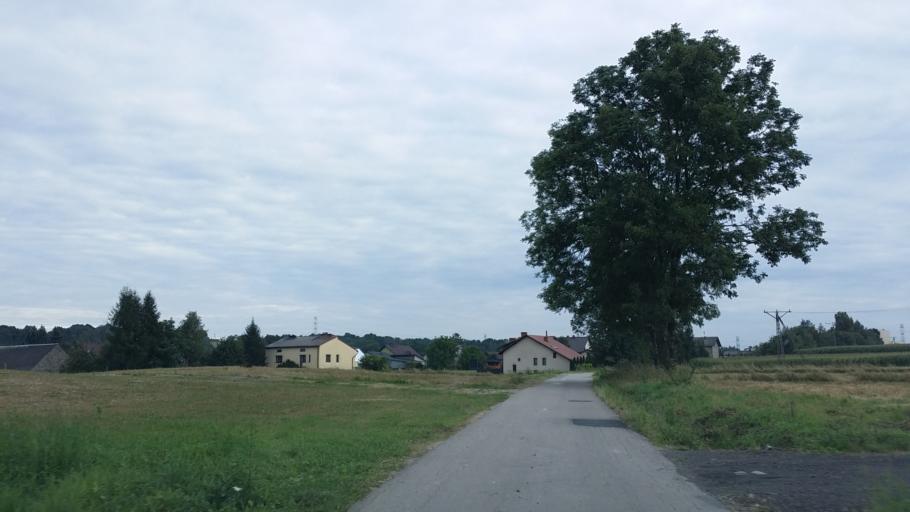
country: PL
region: Lesser Poland Voivodeship
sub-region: Powiat wadowicki
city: Spytkowice
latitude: 49.9931
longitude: 19.4992
